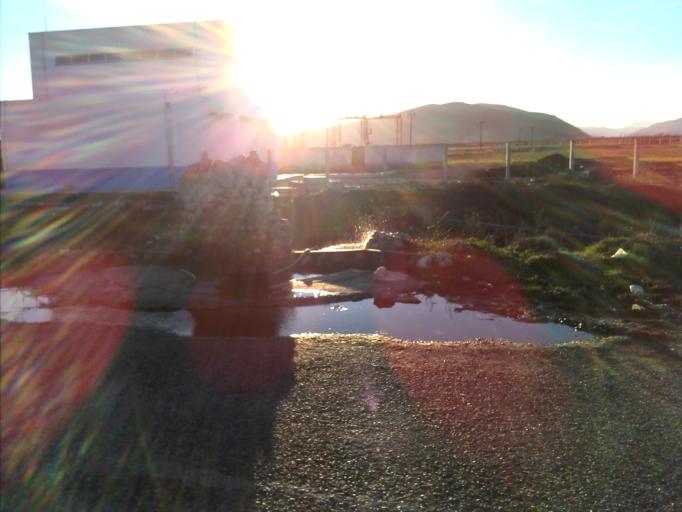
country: AL
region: Shkoder
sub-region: Rrethi i Shkodres
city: Dajc
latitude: 41.9414
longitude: 19.4453
